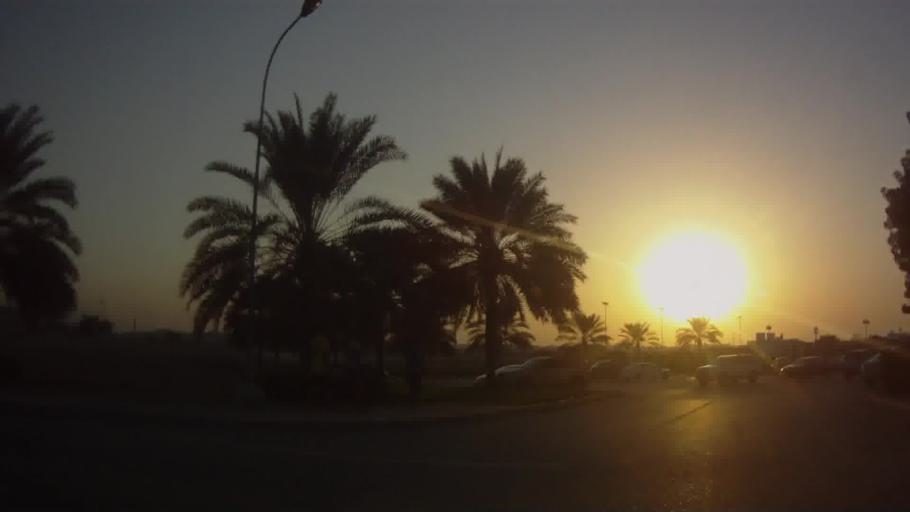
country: OM
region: Muhafazat Masqat
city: Bawshar
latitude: 23.5998
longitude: 58.4031
